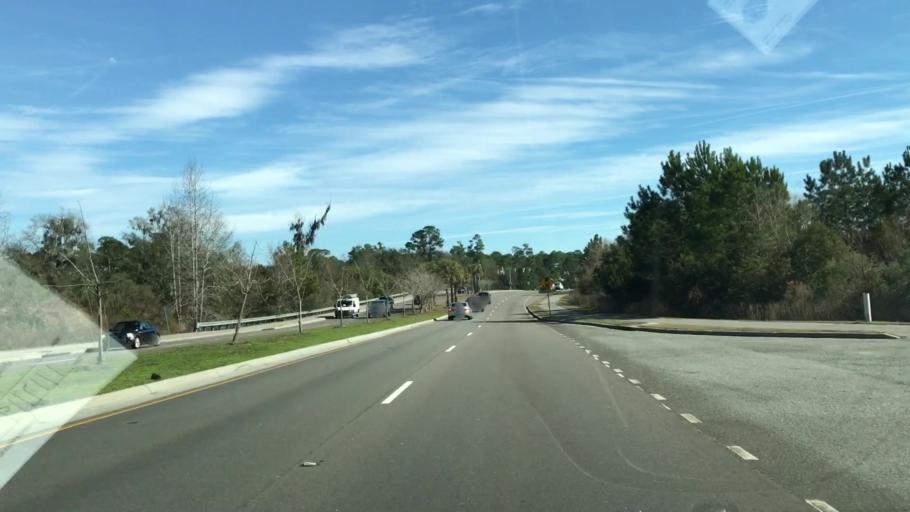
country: US
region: South Carolina
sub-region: Beaufort County
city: Bluffton
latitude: 32.2623
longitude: -80.8737
